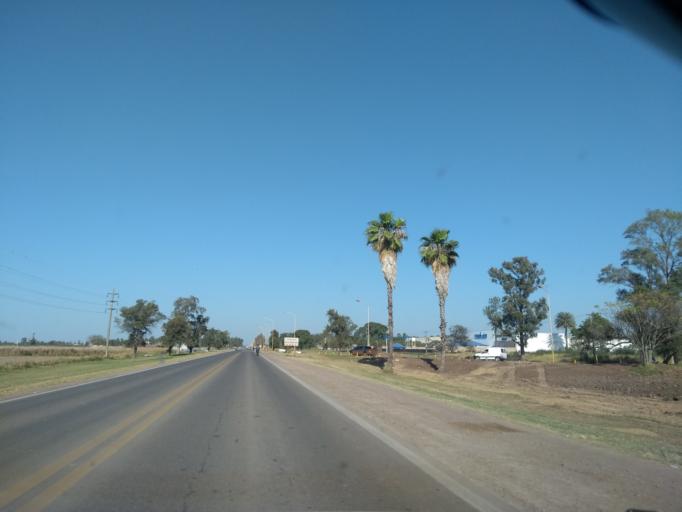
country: AR
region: Chaco
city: Presidencia Roque Saenz Pena
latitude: -26.7993
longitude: -60.4126
